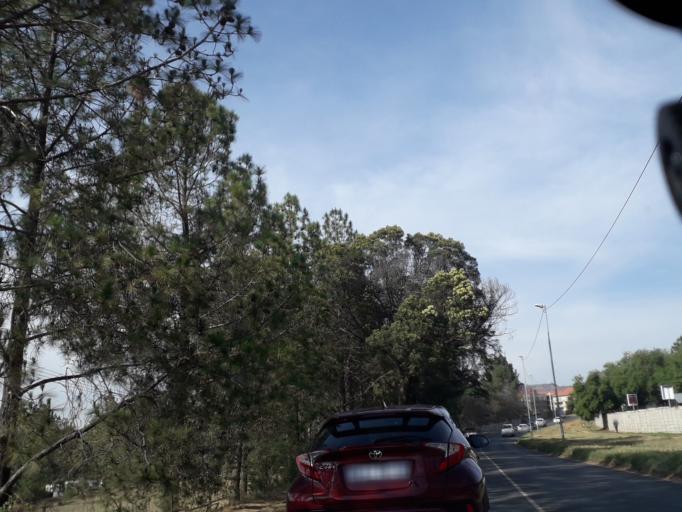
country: ZA
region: Gauteng
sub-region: West Rand District Municipality
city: Muldersdriseloop
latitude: -26.0793
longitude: 27.8798
